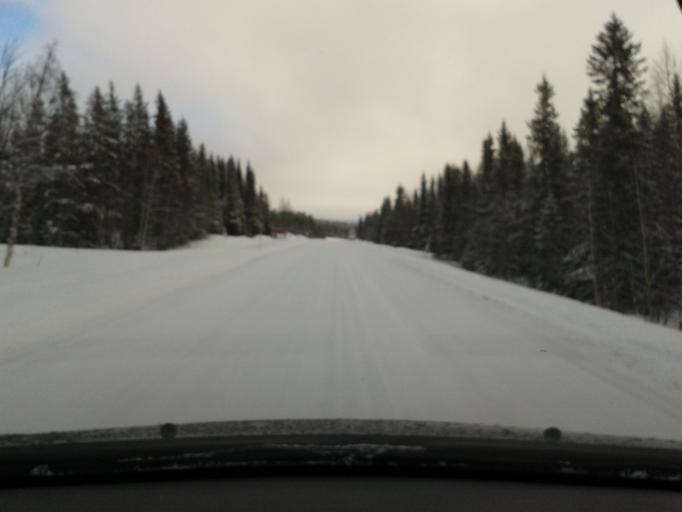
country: SE
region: Vaesterbotten
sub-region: Vilhelmina Kommun
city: Sjoberg
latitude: 65.2512
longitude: 15.6051
